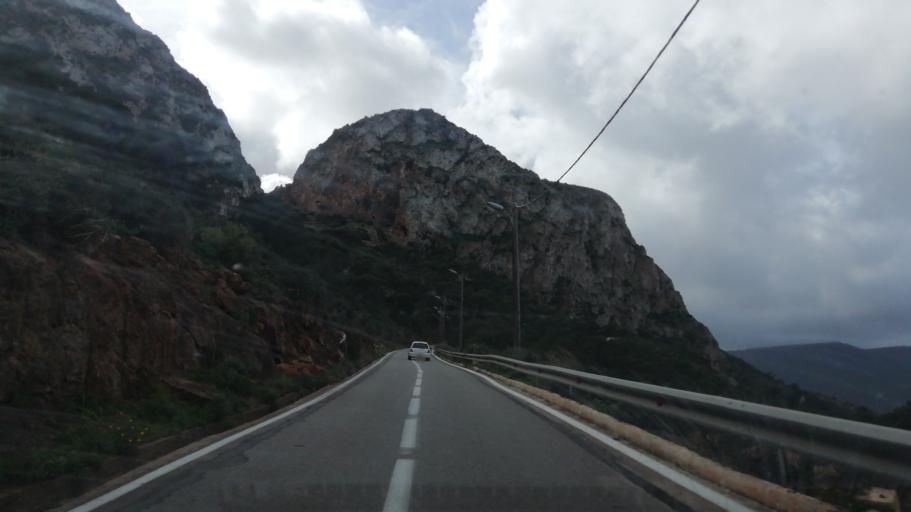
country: DZ
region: Oran
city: Oran
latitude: 35.7103
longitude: -0.6666
